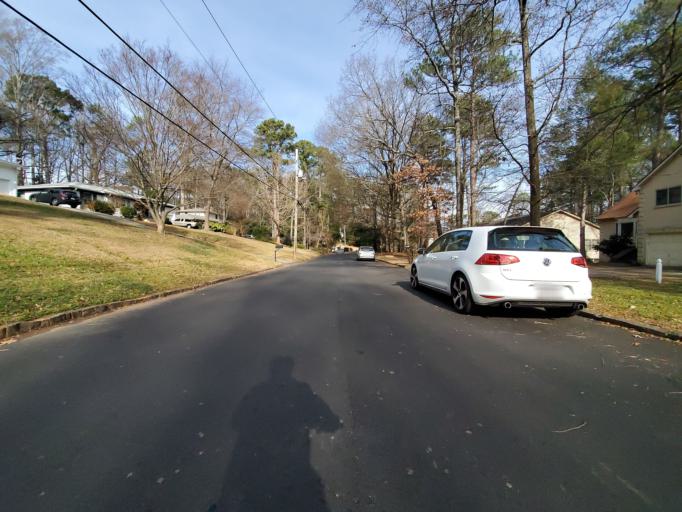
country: US
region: Georgia
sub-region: DeKalb County
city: North Decatur
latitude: 33.7770
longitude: -84.3137
